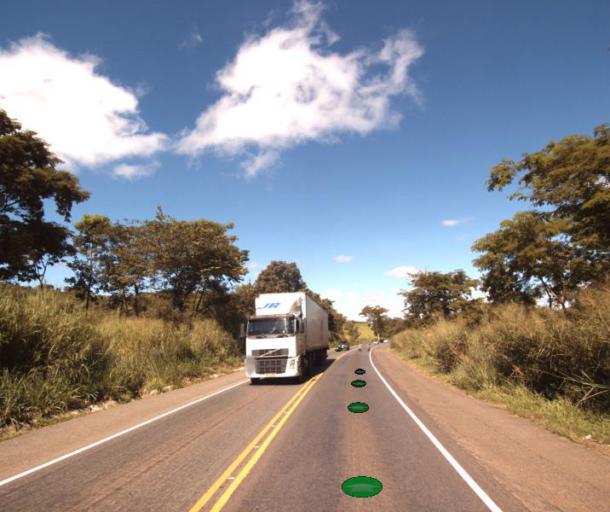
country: BR
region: Goias
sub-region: Rialma
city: Rialma
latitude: -15.2809
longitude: -49.5553
